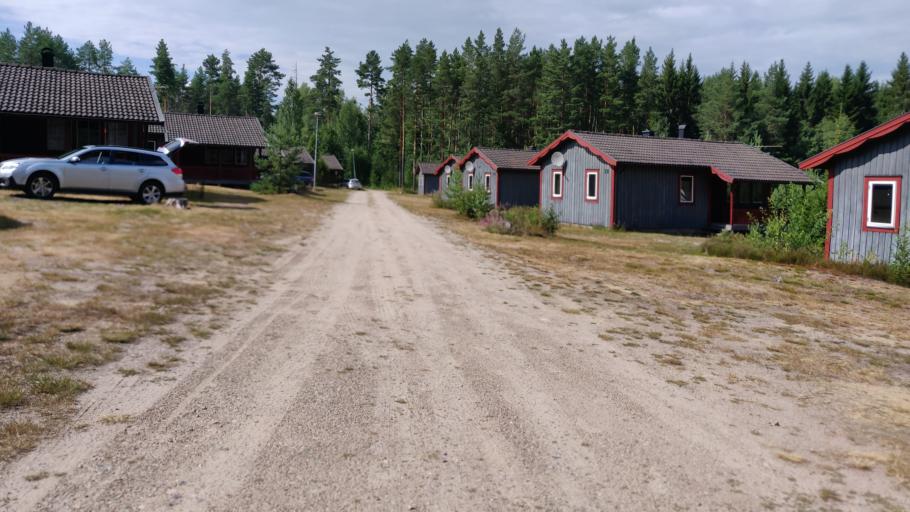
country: SE
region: Vaermland
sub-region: Hagfors Kommun
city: Hagfors
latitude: 60.0157
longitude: 13.5996
